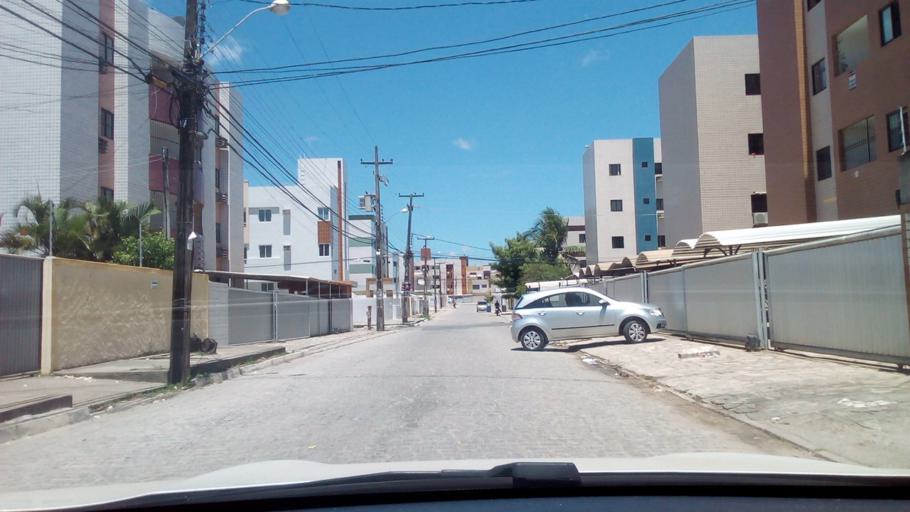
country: BR
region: Paraiba
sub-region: Joao Pessoa
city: Joao Pessoa
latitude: -7.1551
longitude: -34.8346
